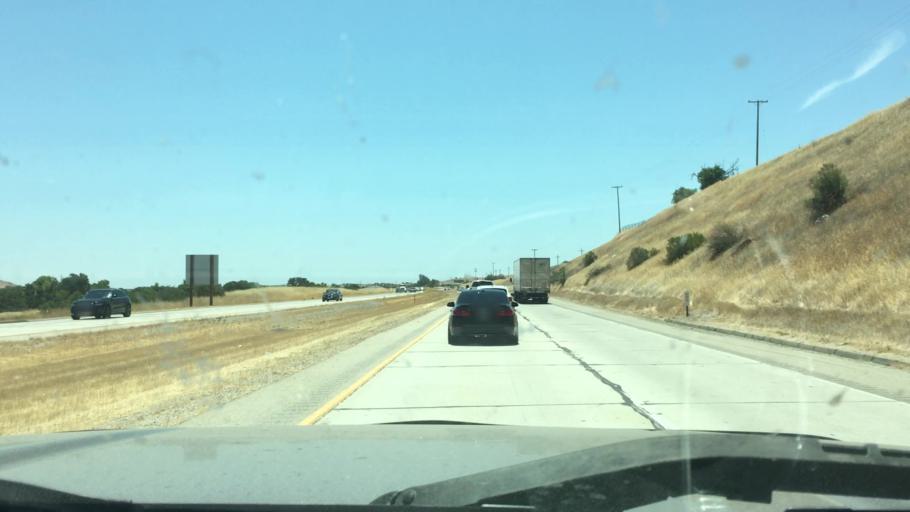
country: US
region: California
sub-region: San Luis Obispo County
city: San Miguel
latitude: 35.8101
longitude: -120.7517
